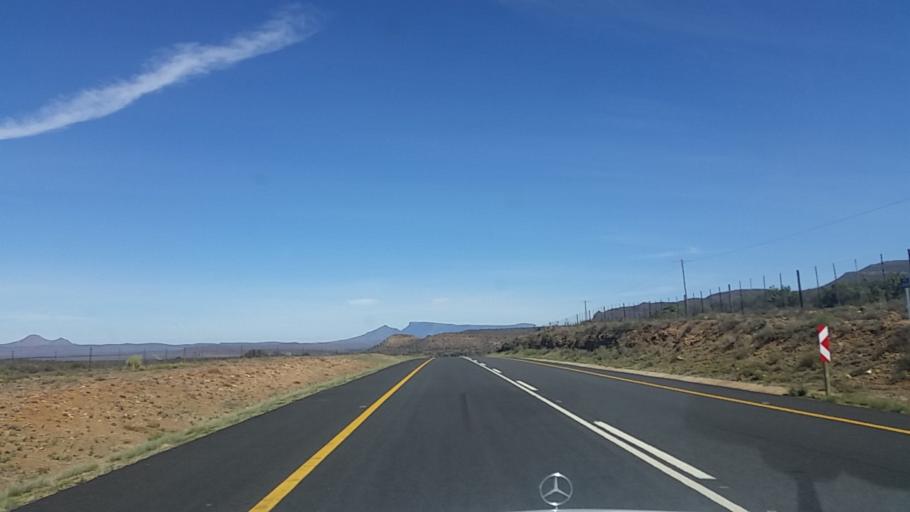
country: ZA
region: Eastern Cape
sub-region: Cacadu District Municipality
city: Graaff-Reinet
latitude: -32.2985
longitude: 24.5167
